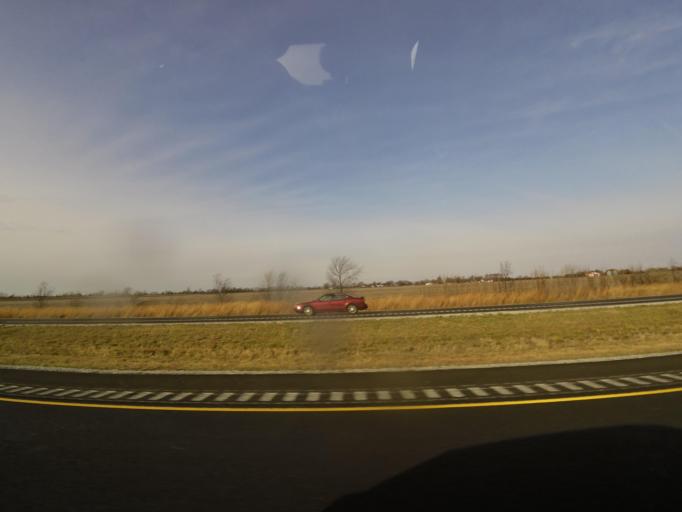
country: US
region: Illinois
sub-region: Macon County
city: Macon
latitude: 39.7696
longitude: -88.9714
